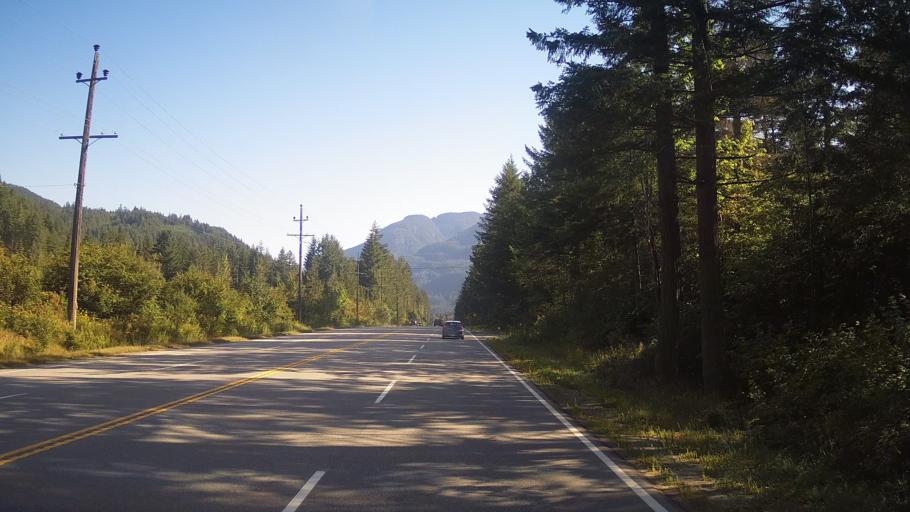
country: CA
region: British Columbia
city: Hope
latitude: 49.4684
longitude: -121.4300
